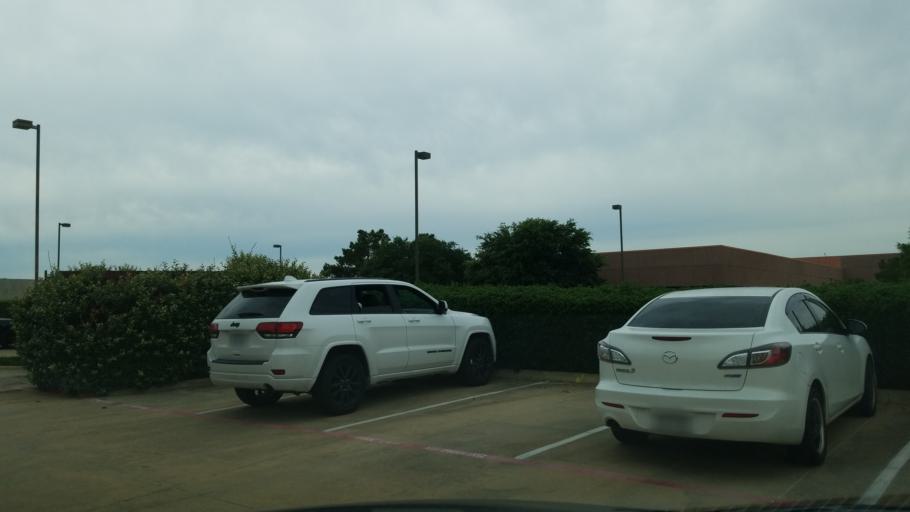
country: US
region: Texas
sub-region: Dallas County
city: Coppell
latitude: 32.8955
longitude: -96.9870
